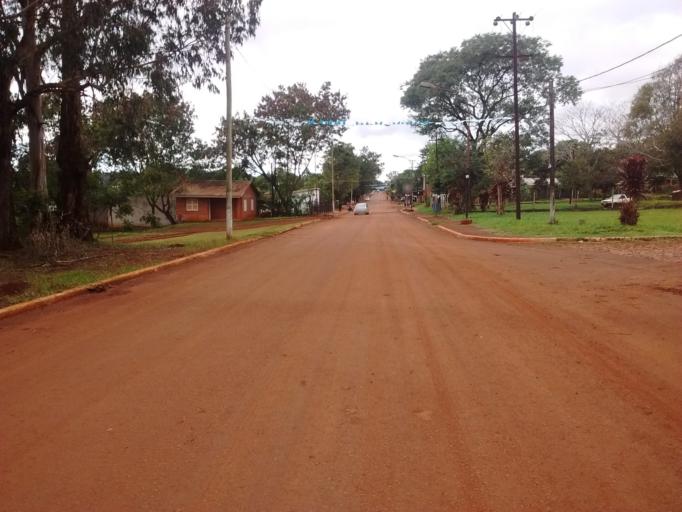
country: AR
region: Misiones
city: Puerto Libertad
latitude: -25.9207
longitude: -54.5891
